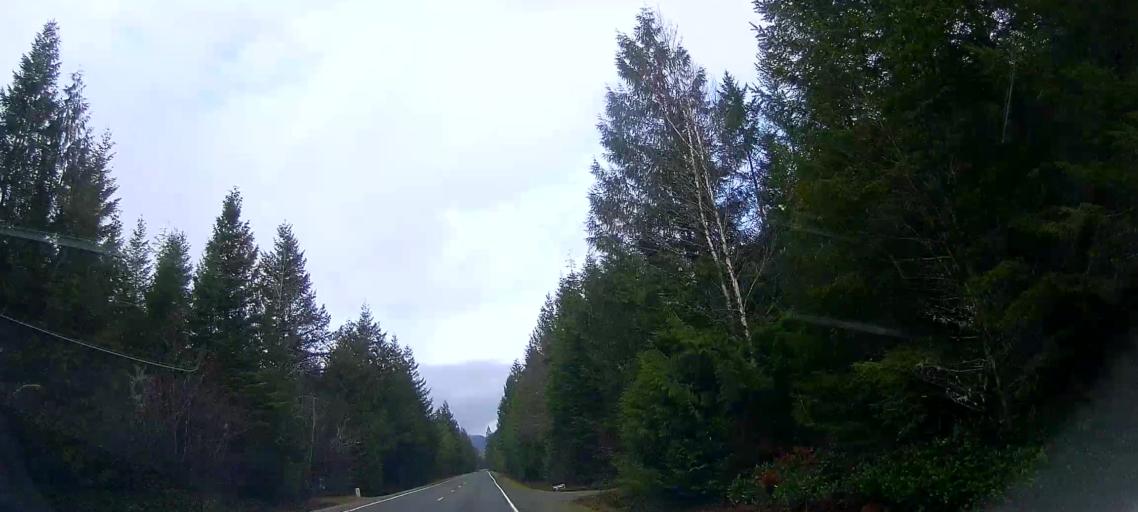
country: US
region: Washington
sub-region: Snohomish County
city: Darrington
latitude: 48.5082
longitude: -121.4572
